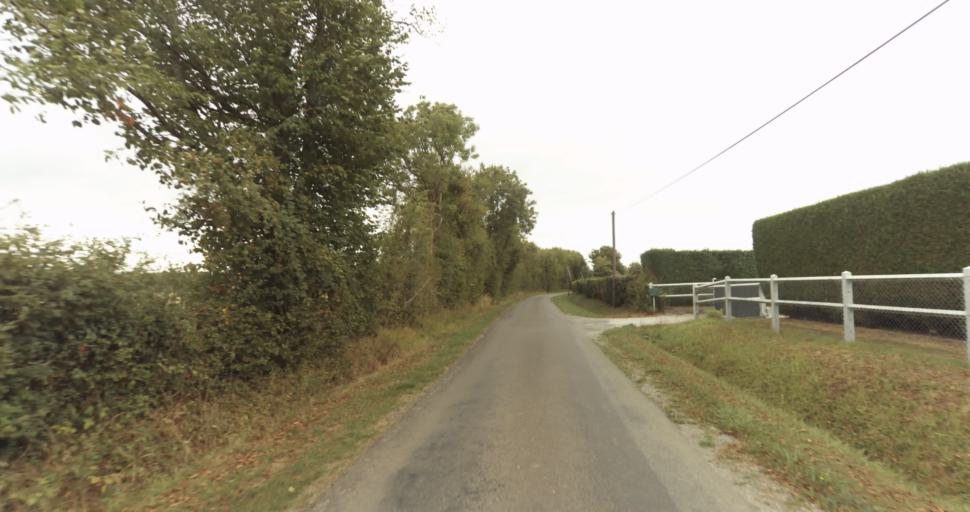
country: FR
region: Lower Normandy
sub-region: Departement de l'Orne
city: Gace
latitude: 48.8510
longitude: 0.3211
